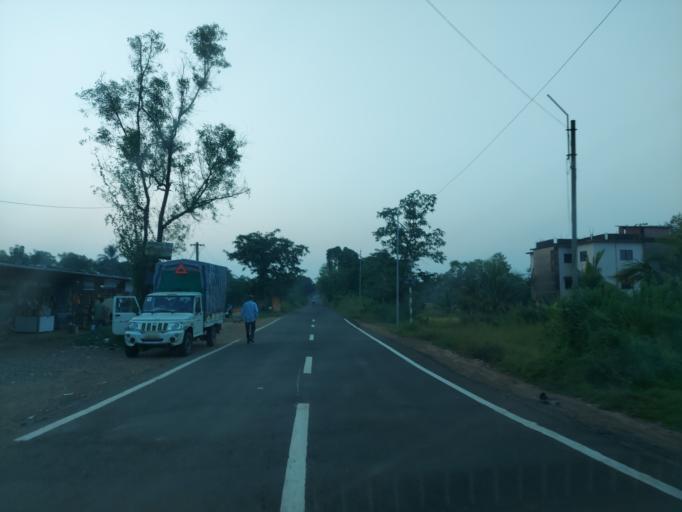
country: IN
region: Maharashtra
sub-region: Sindhudurg
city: Kudal
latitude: 16.1036
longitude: 73.7086
